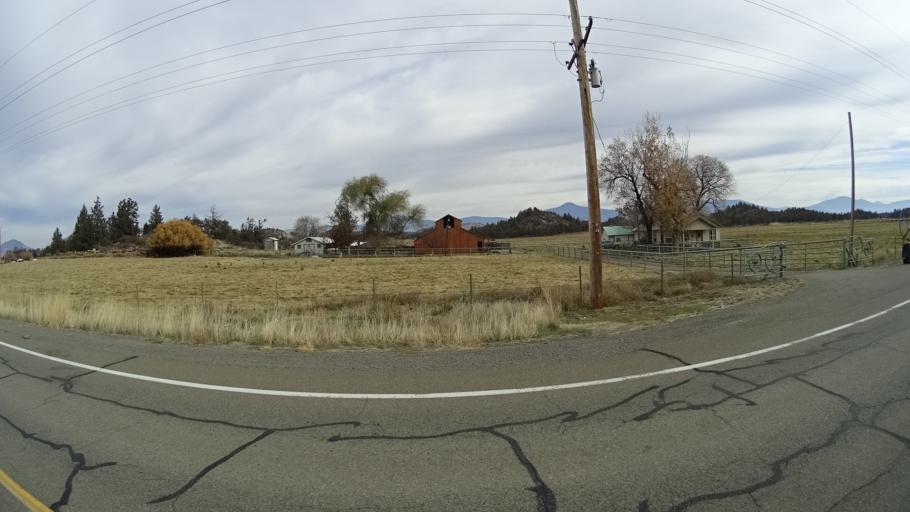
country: US
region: California
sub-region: Siskiyou County
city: Montague
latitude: 41.6776
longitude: -122.5274
